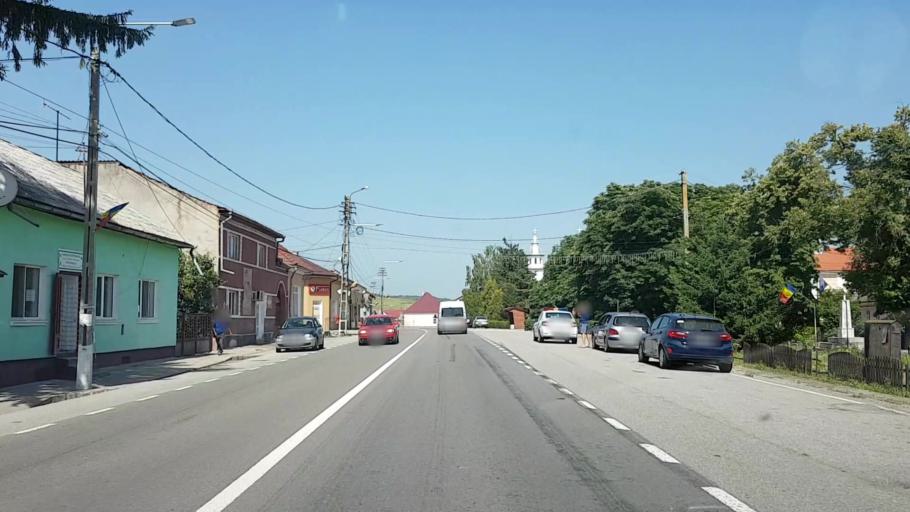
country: RO
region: Bistrita-Nasaud
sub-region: Comuna Petru Rares
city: Reteag
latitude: 47.1951
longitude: 24.0163
